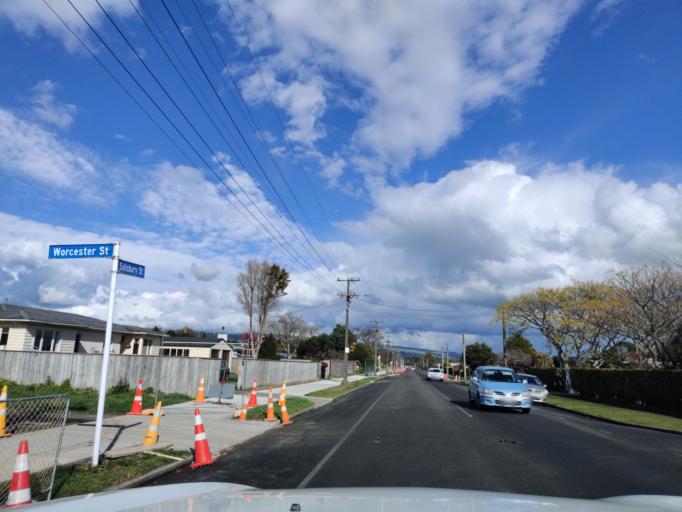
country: NZ
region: Manawatu-Wanganui
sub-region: Palmerston North City
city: Palmerston North
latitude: -40.2860
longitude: 175.7593
